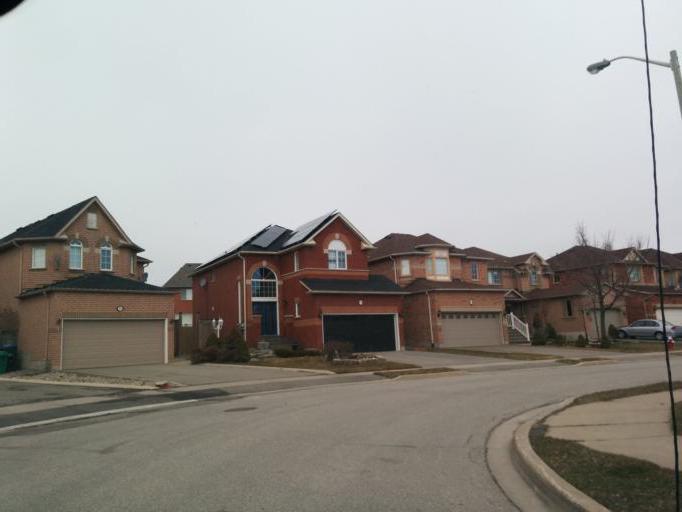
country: CA
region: Ontario
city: Brampton
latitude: 43.7295
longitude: -79.8249
